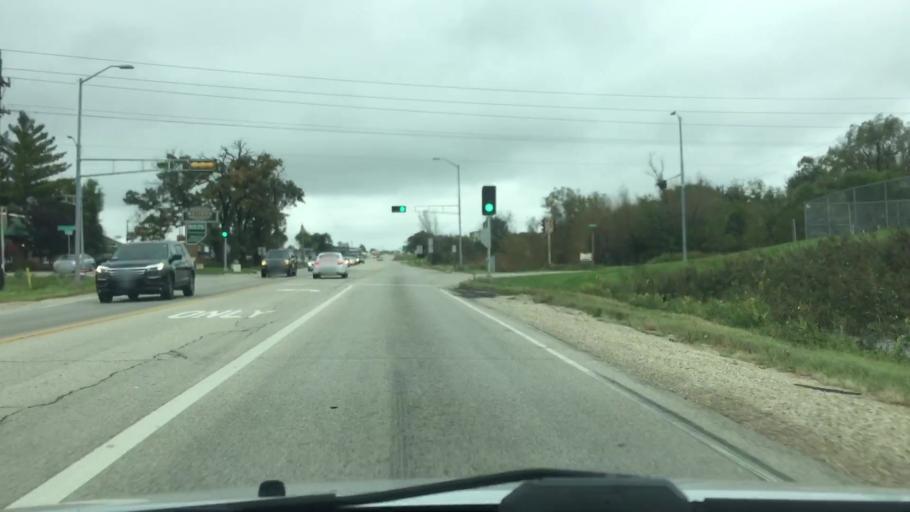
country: US
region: Wisconsin
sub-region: Walworth County
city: Elkhorn
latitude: 42.7067
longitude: -88.5421
